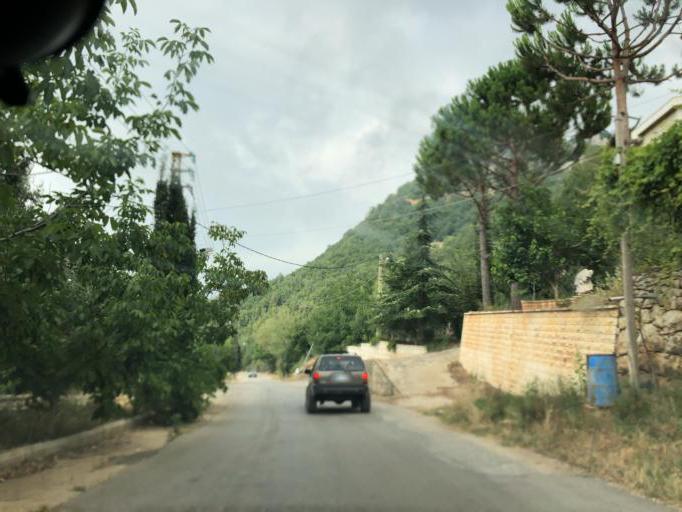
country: LB
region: Mont-Liban
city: Jbail
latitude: 34.0714
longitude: 35.8595
